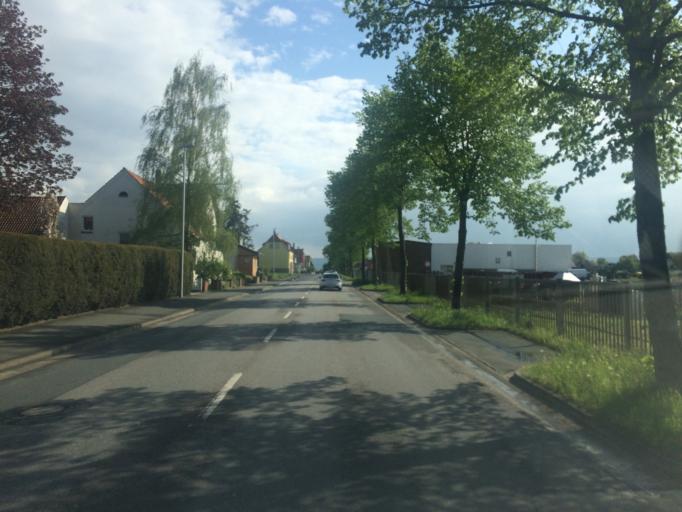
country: DE
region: Lower Saxony
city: Gross Munzel
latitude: 52.3700
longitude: 9.4793
